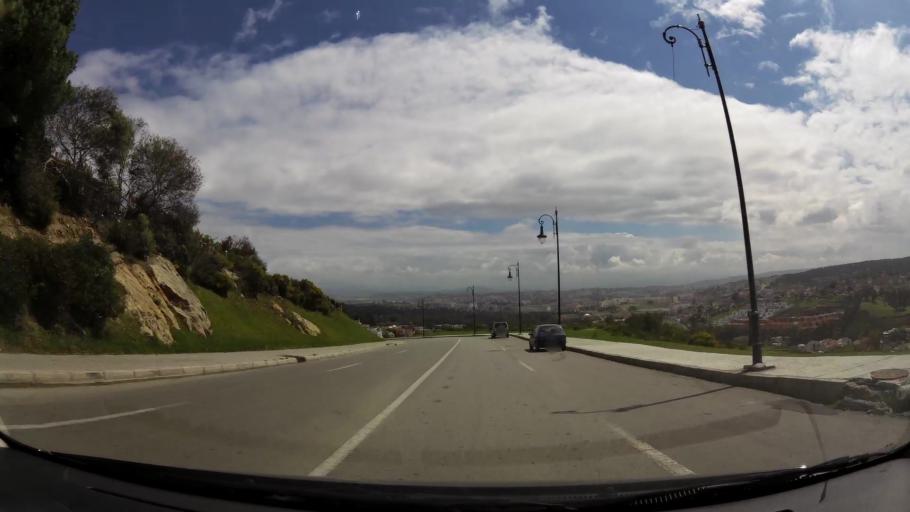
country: MA
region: Tanger-Tetouan
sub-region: Tanger-Assilah
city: Boukhalef
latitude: 35.7831
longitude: -5.8642
